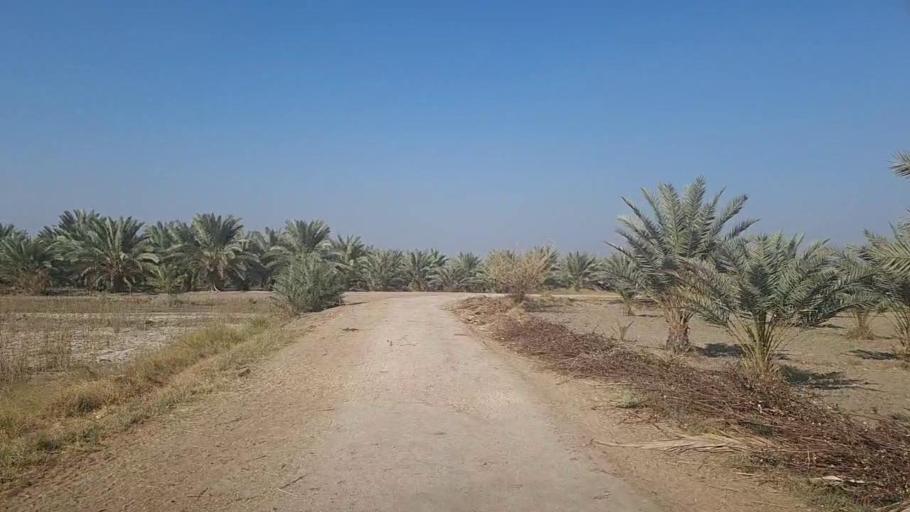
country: PK
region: Sindh
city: Kot Diji
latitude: 27.4342
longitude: 68.7376
